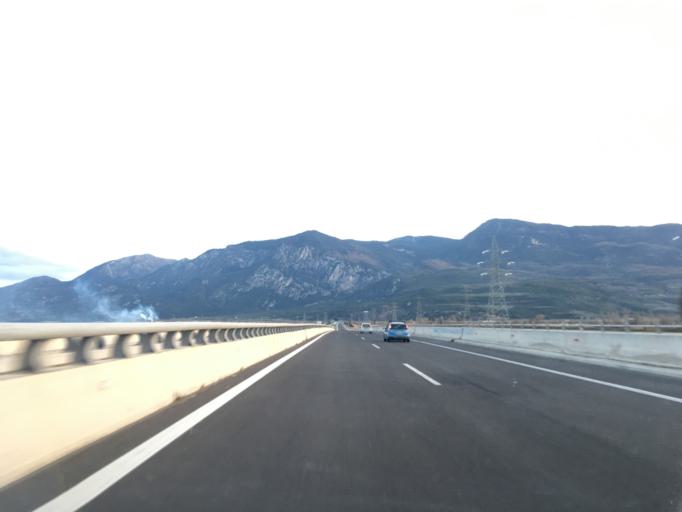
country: GR
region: Central Greece
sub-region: Nomos Fthiotidos
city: Anthili
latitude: 38.8285
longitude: 22.4843
